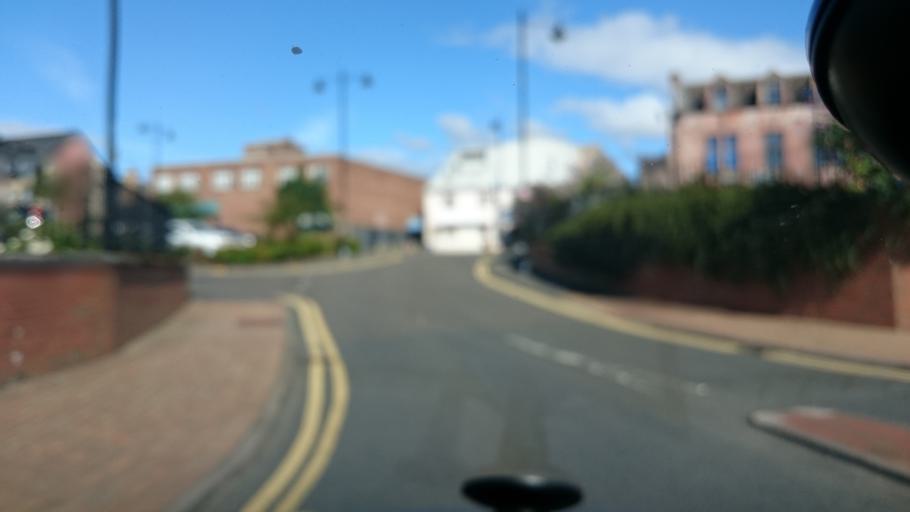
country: GB
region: Scotland
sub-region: Clackmannanshire
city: Alloa
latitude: 56.1143
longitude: -3.7896
